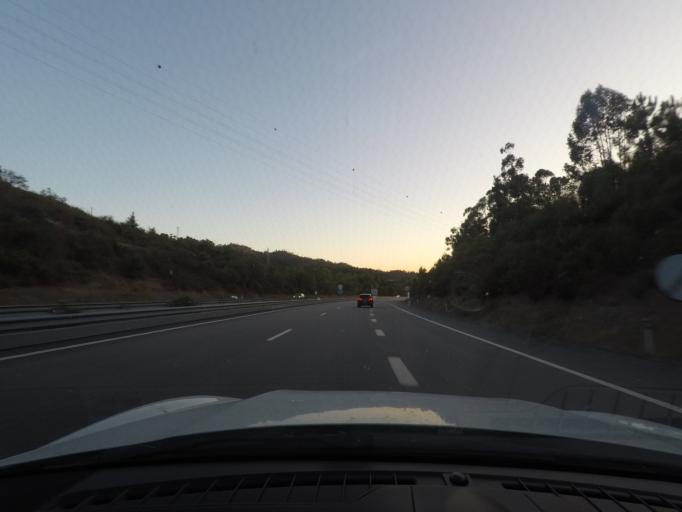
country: PT
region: Braga
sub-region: Fafe
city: Fafe
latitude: 41.4283
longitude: -8.1835
